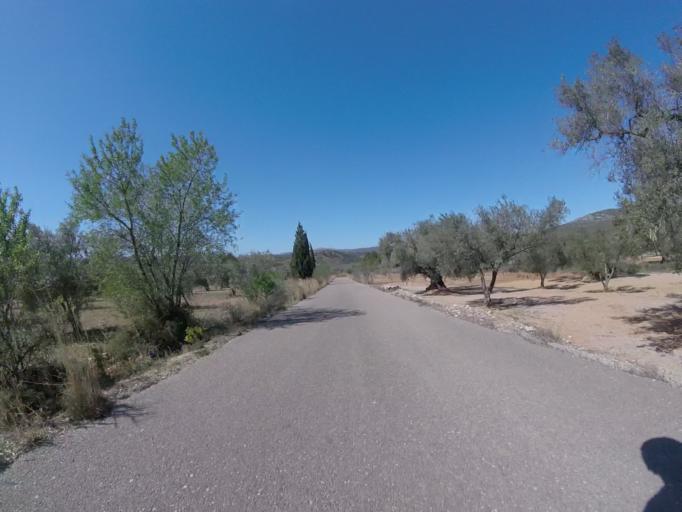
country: ES
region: Valencia
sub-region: Provincia de Castello
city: Cuevas de Vinroma
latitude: 40.3840
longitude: 0.1480
